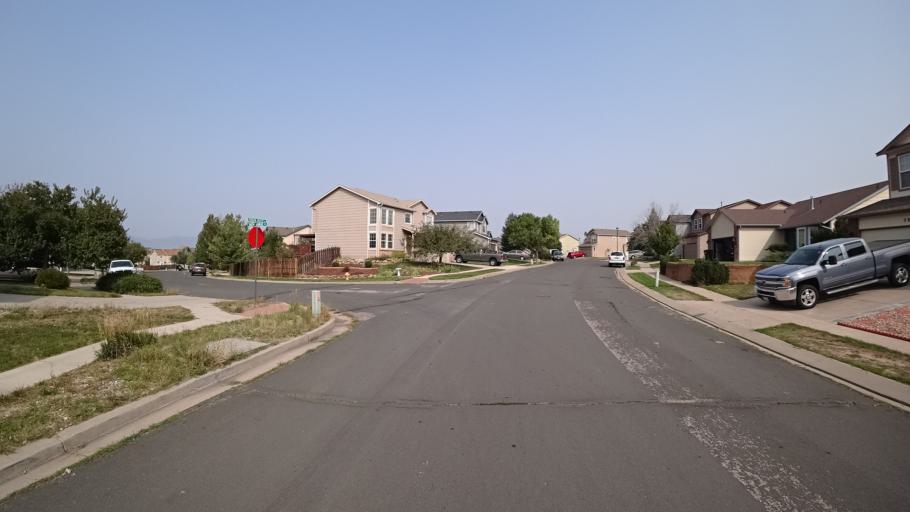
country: US
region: Colorado
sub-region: El Paso County
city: Cimarron Hills
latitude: 38.9259
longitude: -104.7341
